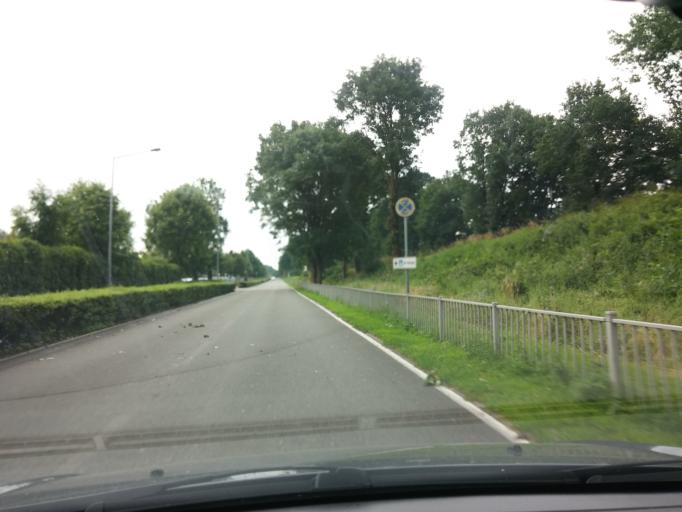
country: DE
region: North Rhine-Westphalia
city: Dorsten
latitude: 51.6248
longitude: 6.9706
